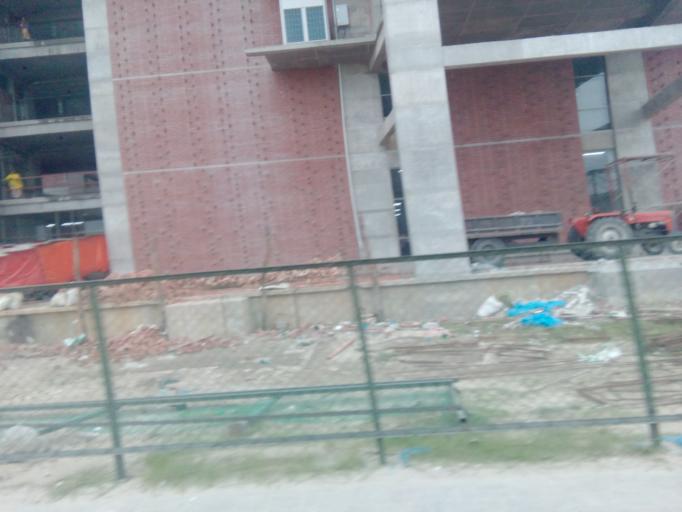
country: BD
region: Dhaka
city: Paltan
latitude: 23.7977
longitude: 90.4494
